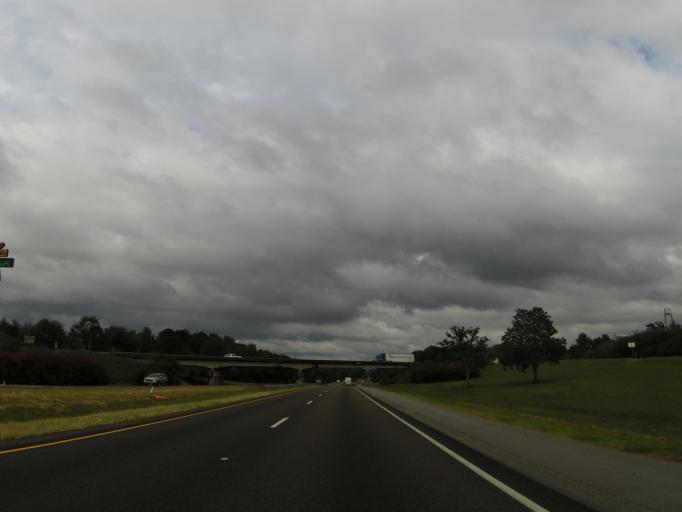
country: US
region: Alabama
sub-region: Conecuh County
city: Evergreen
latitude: 31.4177
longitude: -87.0071
